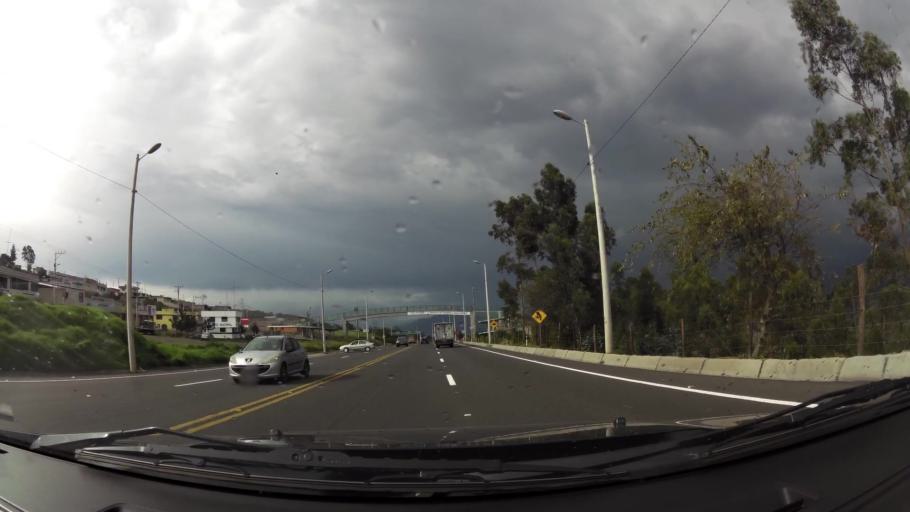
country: EC
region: Pichincha
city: Sangolqui
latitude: -0.3878
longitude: -78.5357
